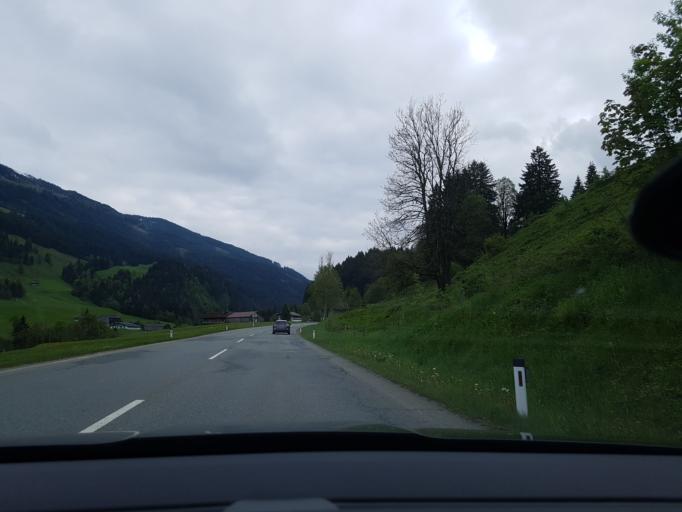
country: AT
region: Tyrol
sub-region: Politischer Bezirk Kitzbuhel
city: Jochberg
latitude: 47.3600
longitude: 12.4139
